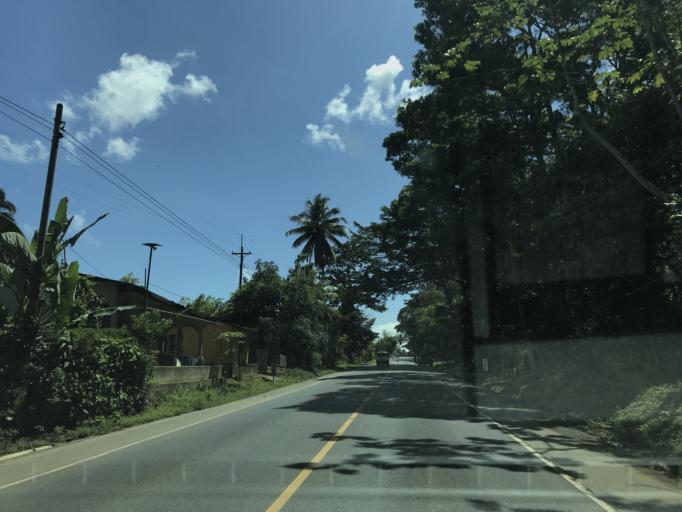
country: GT
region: Izabal
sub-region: Municipio de Puerto Barrios
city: Puerto Barrios
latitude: 15.6633
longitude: -88.5549
